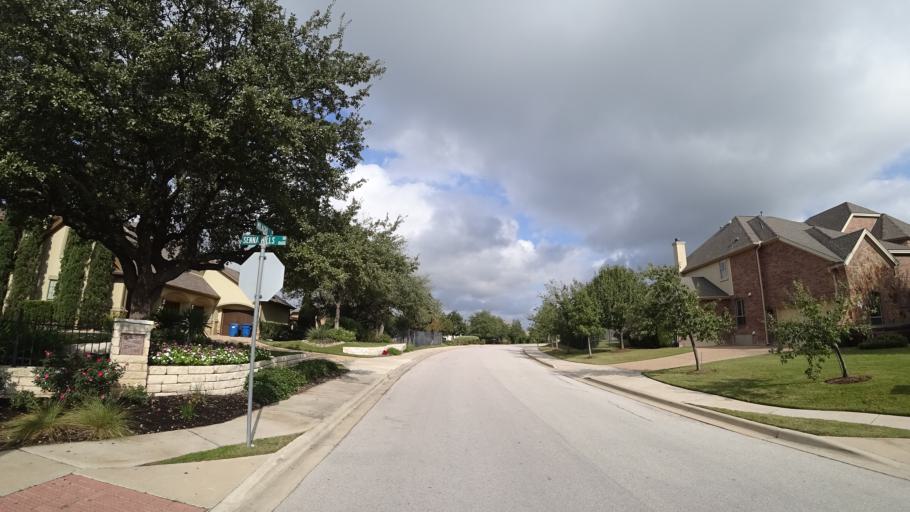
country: US
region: Texas
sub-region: Travis County
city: Barton Creek
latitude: 30.3125
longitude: -97.8999
